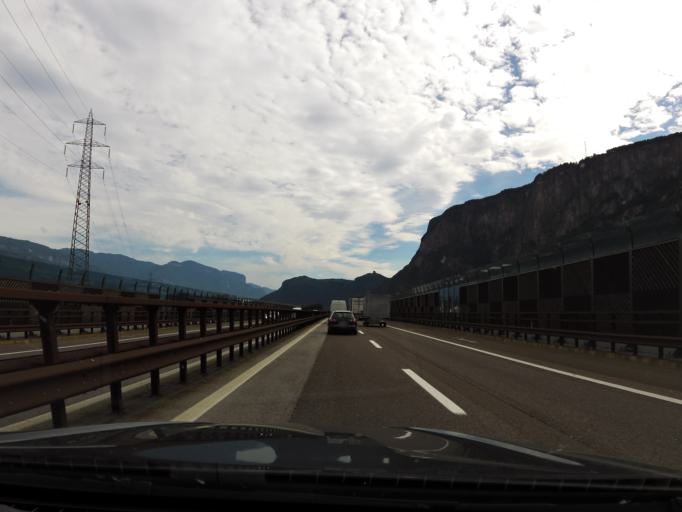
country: IT
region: Trentino-Alto Adige
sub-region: Bolzano
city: Vadena
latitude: 46.4128
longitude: 11.3073
